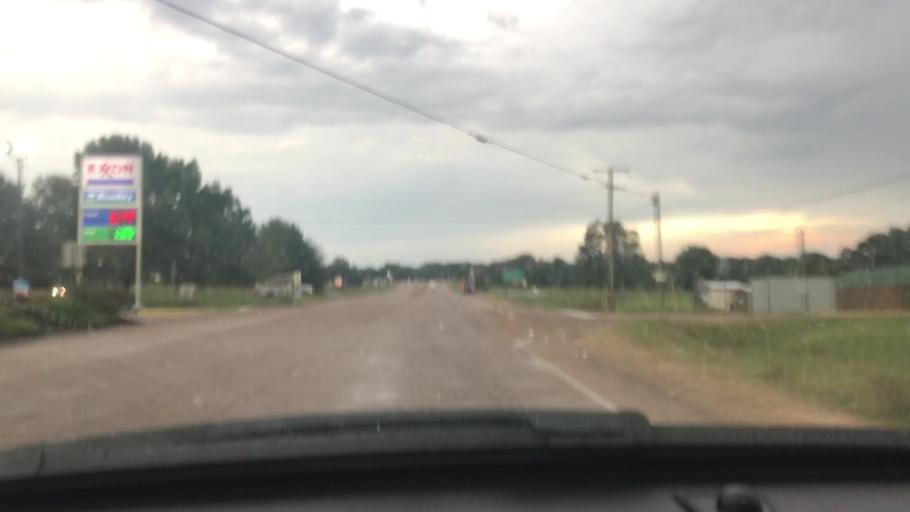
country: US
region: Mississippi
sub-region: Pike County
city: Summit
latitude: 31.2895
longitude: -90.4830
